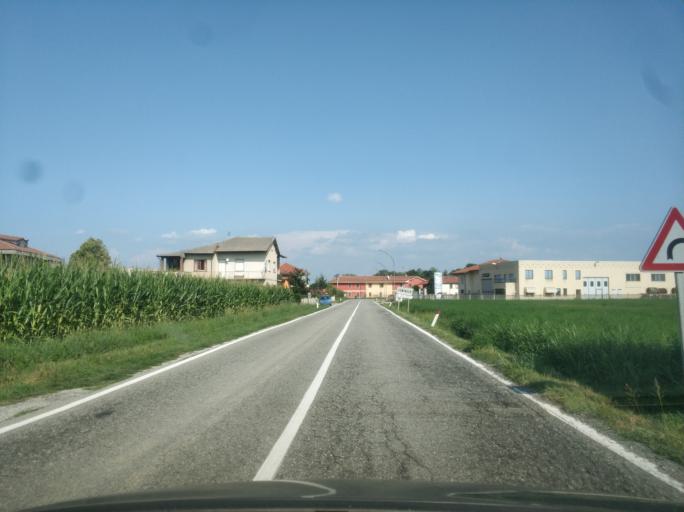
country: IT
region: Piedmont
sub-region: Provincia di Cuneo
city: Centallo
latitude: 44.5035
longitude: 7.5777
